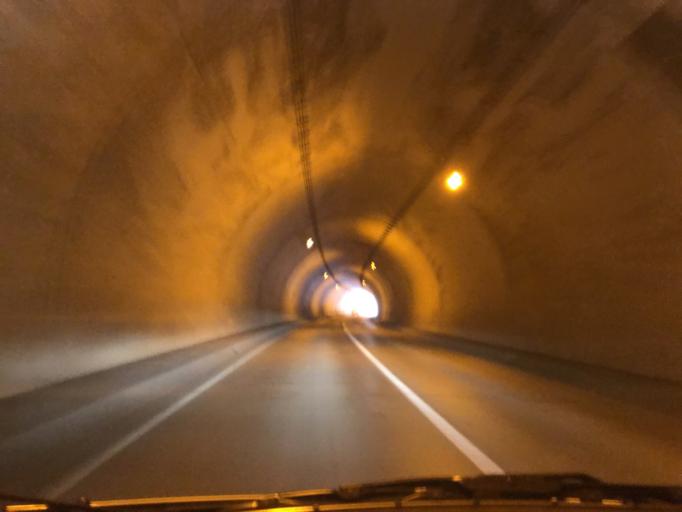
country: JP
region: Iwate
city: Hanamaki
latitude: 39.3691
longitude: 141.1648
